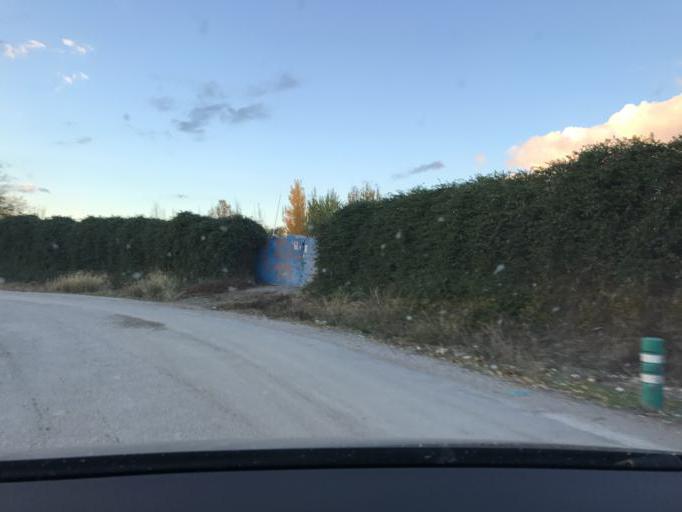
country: ES
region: Andalusia
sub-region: Provincia de Granada
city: Churriana de la Vega
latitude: 37.1718
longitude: -3.6487
